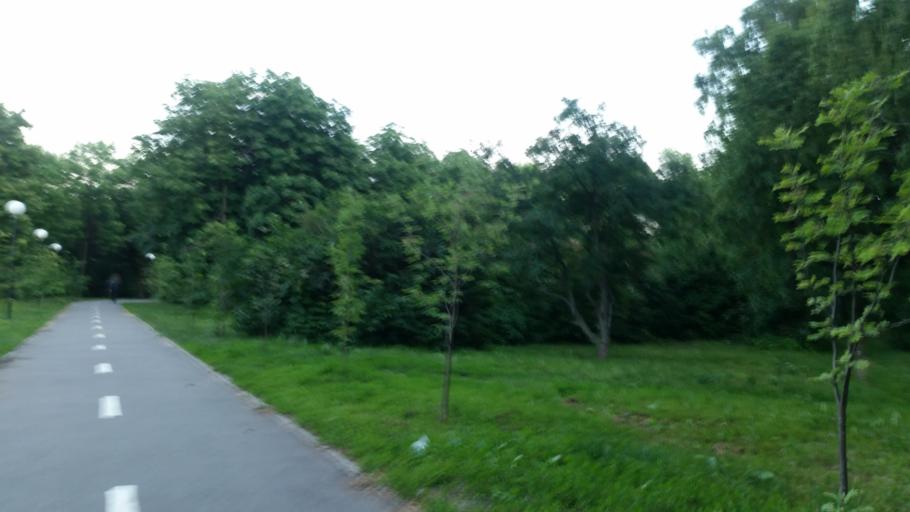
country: RU
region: Ulyanovsk
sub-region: Ulyanovskiy Rayon
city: Ulyanovsk
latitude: 54.3294
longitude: 48.4071
